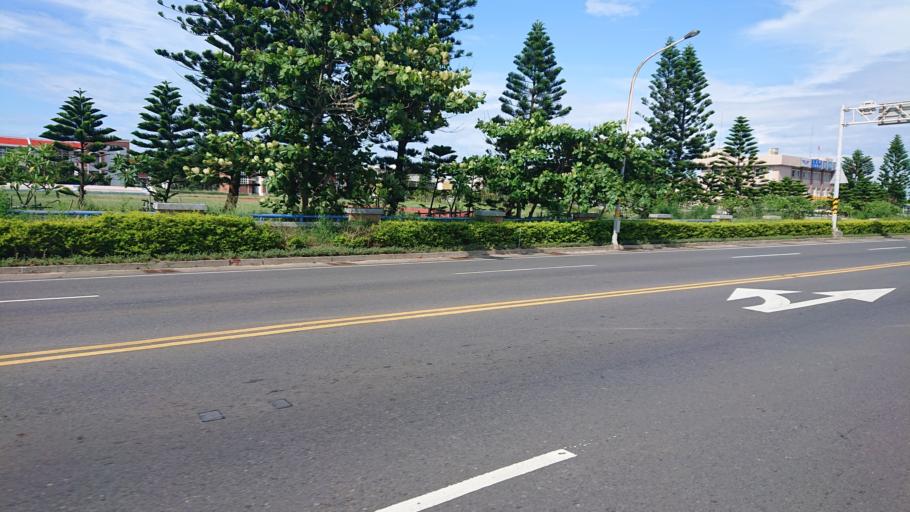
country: TW
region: Taiwan
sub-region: Penghu
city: Ma-kung
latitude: 23.5591
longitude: 119.5991
